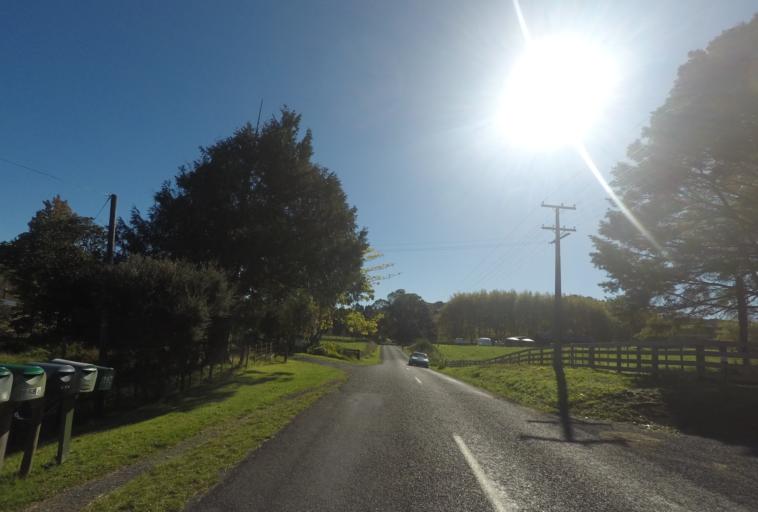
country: NZ
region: Bay of Plenty
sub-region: Western Bay of Plenty District
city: Waihi Beach
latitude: -37.3994
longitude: 175.9064
